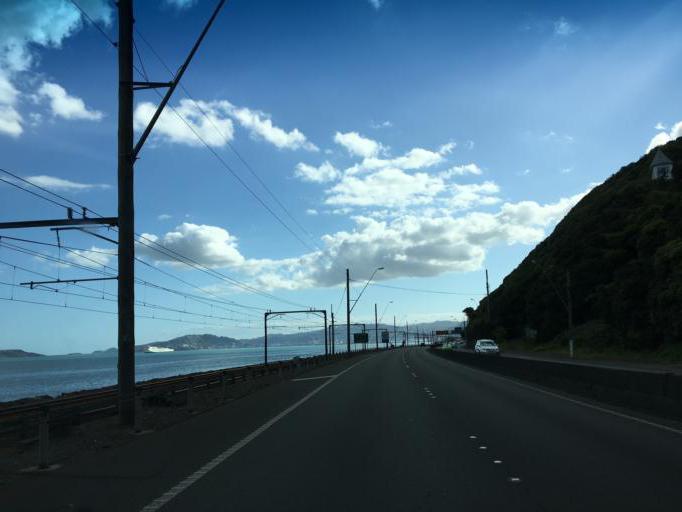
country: NZ
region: Wellington
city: Petone
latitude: -41.2342
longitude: 174.8354
